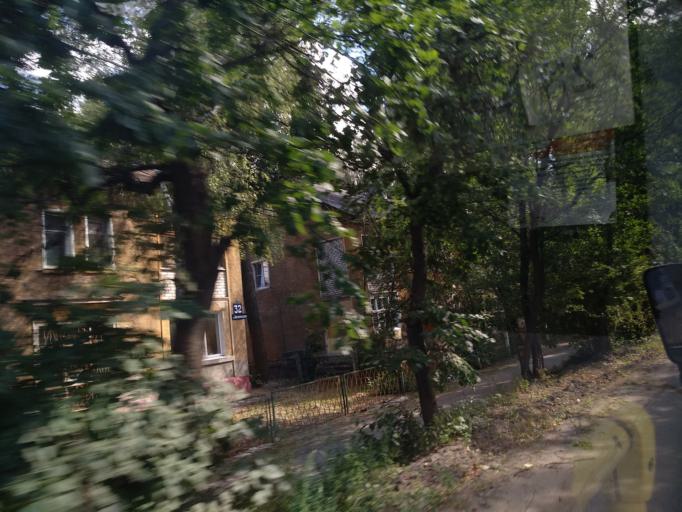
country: RU
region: Nizjnij Novgorod
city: Gorbatovka
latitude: 56.2471
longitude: 43.8291
